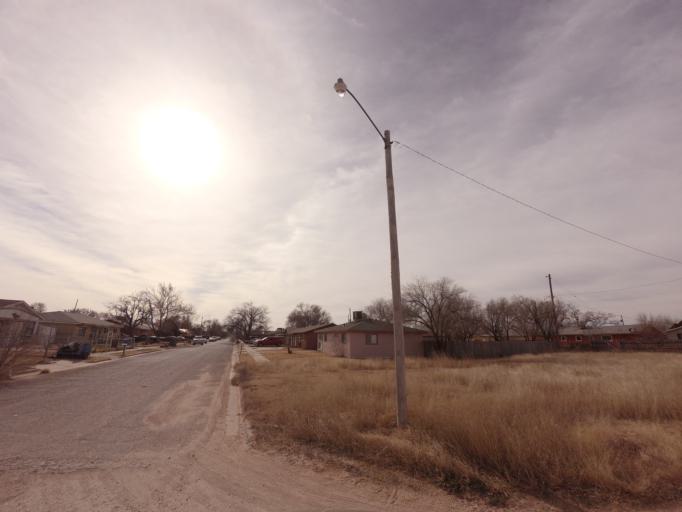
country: US
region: New Mexico
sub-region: Curry County
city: Clovis
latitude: 34.4119
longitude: -103.2386
